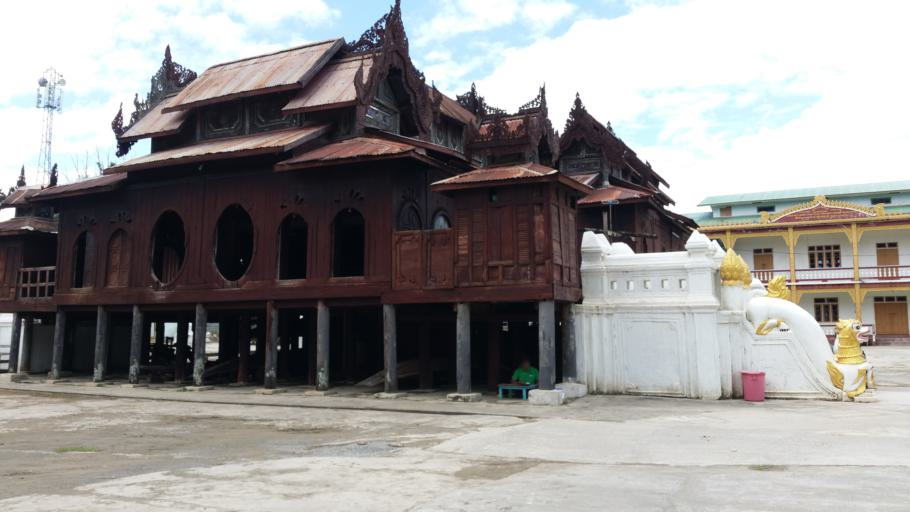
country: MM
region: Shan
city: Taunggyi
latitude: 20.6845
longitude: 96.9319
